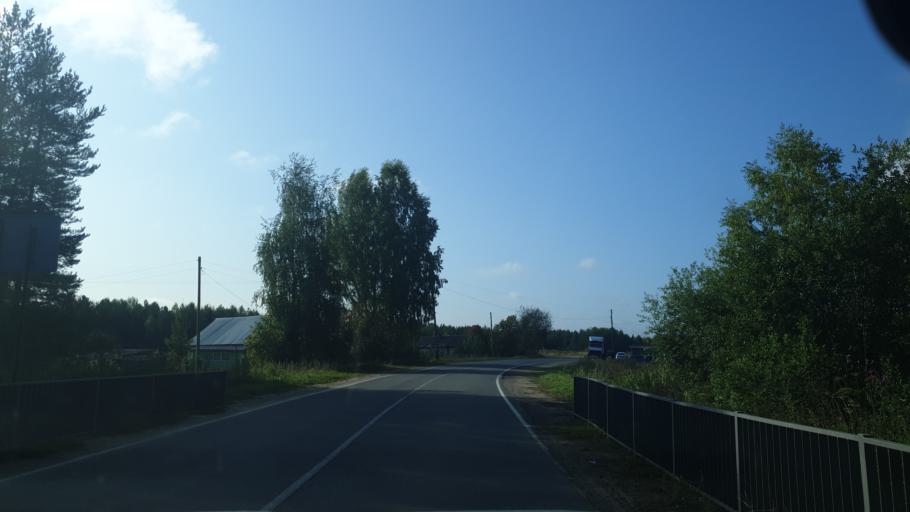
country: RU
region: Komi Republic
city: Vizinga
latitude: 60.9158
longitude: 50.2119
